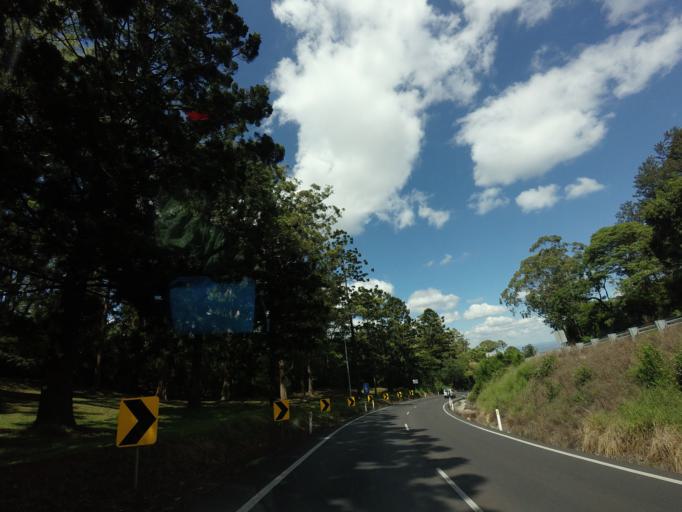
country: AU
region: Queensland
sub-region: Toowoomba
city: East Toowoomba
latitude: -27.5647
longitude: 151.9785
